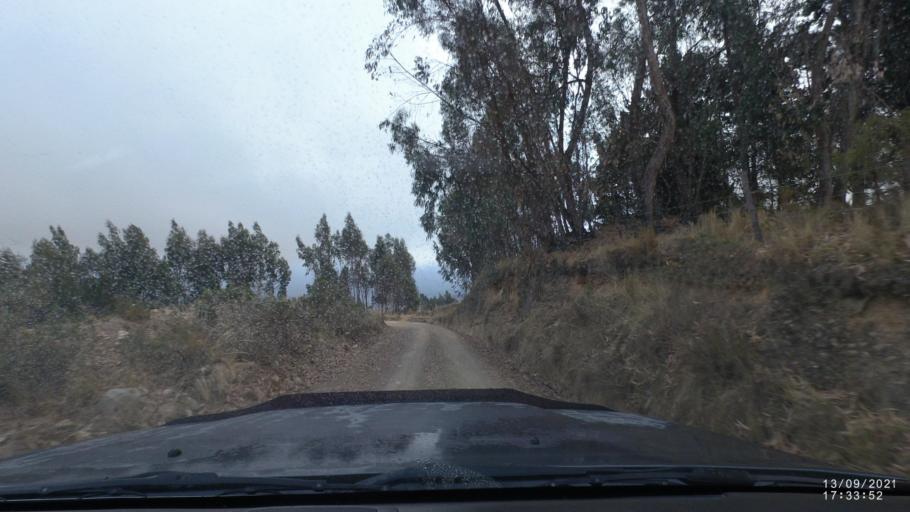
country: BO
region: Cochabamba
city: Colomi
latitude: -17.3663
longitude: -65.7940
